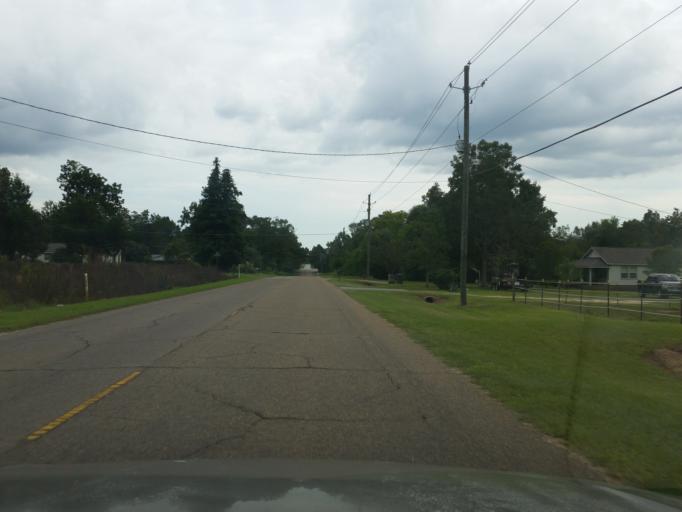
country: US
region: Florida
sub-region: Escambia County
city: Molino
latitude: 30.7224
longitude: -87.3408
